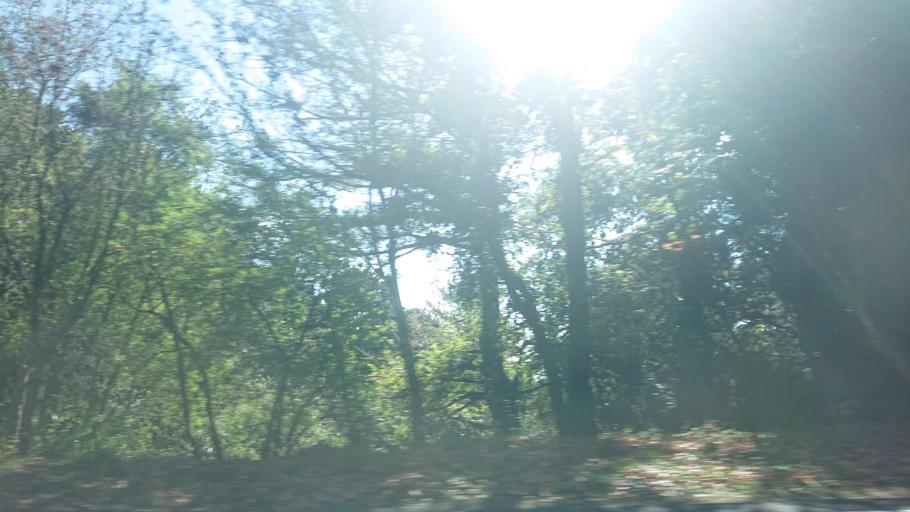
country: TW
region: Taiwan
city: Lugu
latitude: 23.5059
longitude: 120.8191
